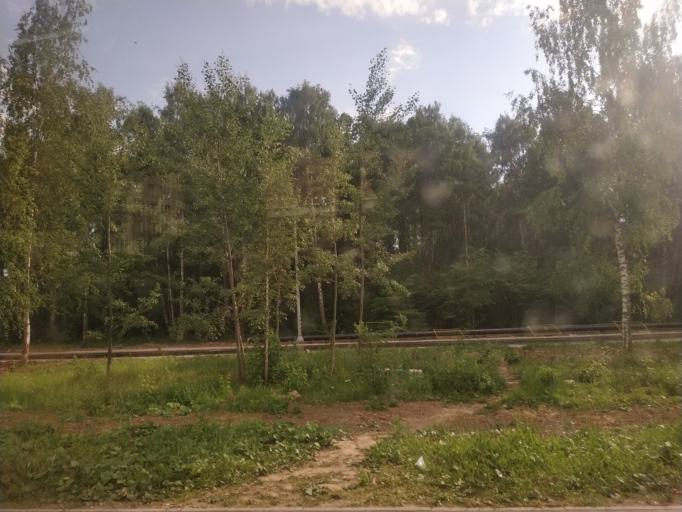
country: RU
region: Moskovskaya
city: Mosrentgen
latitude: 55.5877
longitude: 37.4551
